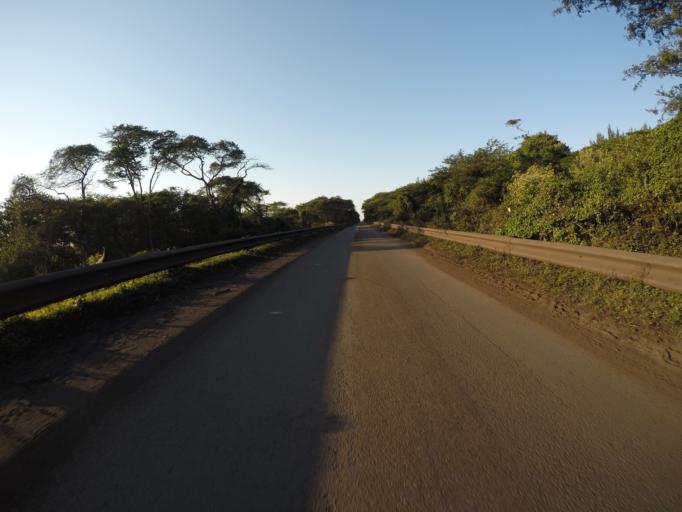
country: ZA
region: KwaZulu-Natal
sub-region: uThungulu District Municipality
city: KwaMbonambi
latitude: -28.6991
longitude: 32.2062
